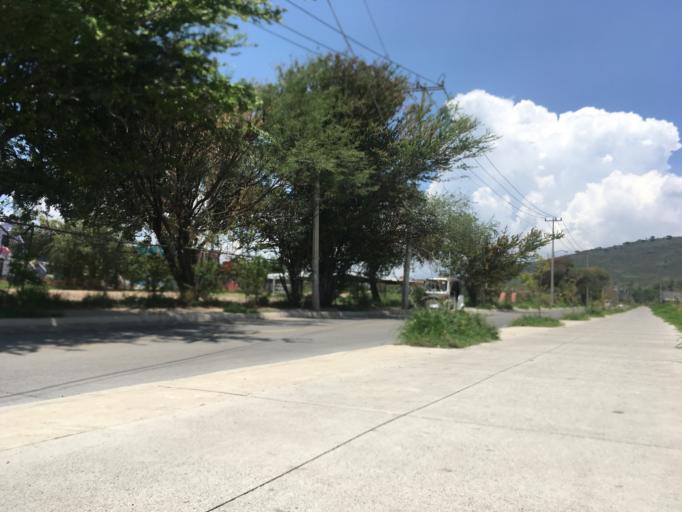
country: MX
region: Jalisco
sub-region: Tlajomulco de Zuniga
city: Jardines de San Sebastian
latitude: 20.5196
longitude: -103.4251
